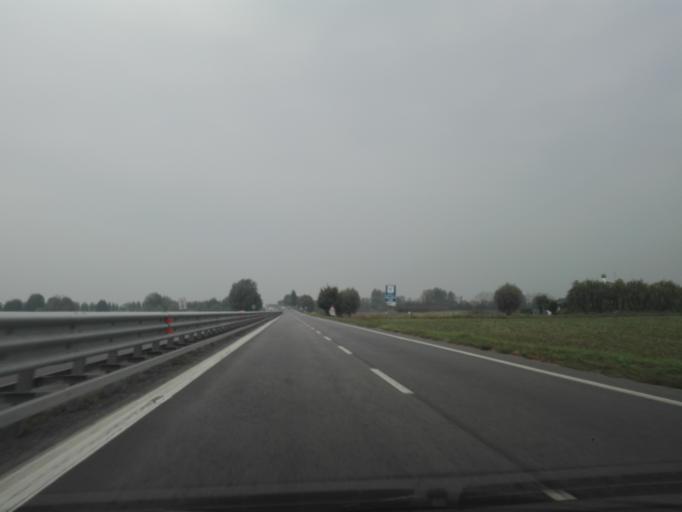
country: IT
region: Veneto
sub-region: Provincia di Verona
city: Legnago
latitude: 45.1718
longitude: 11.2914
